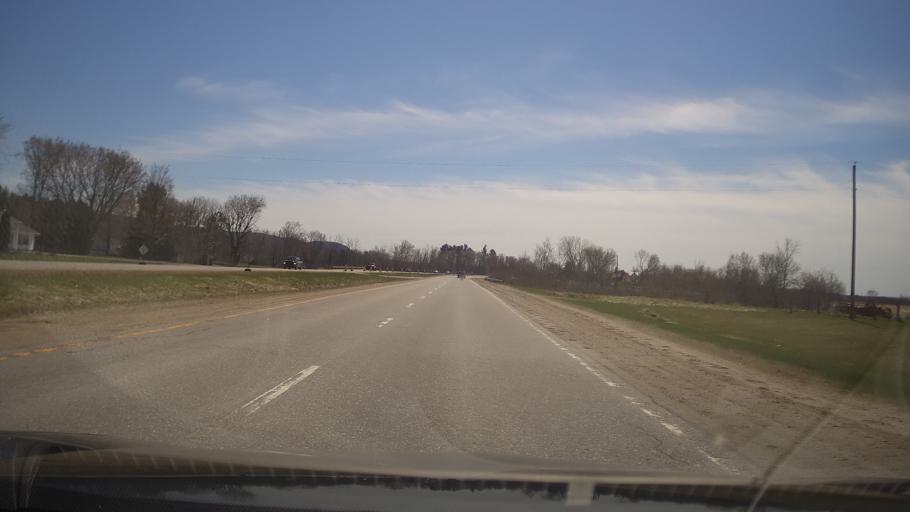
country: CA
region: Quebec
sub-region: Outaouais
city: Wakefield
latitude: 45.5256
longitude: -75.9972
